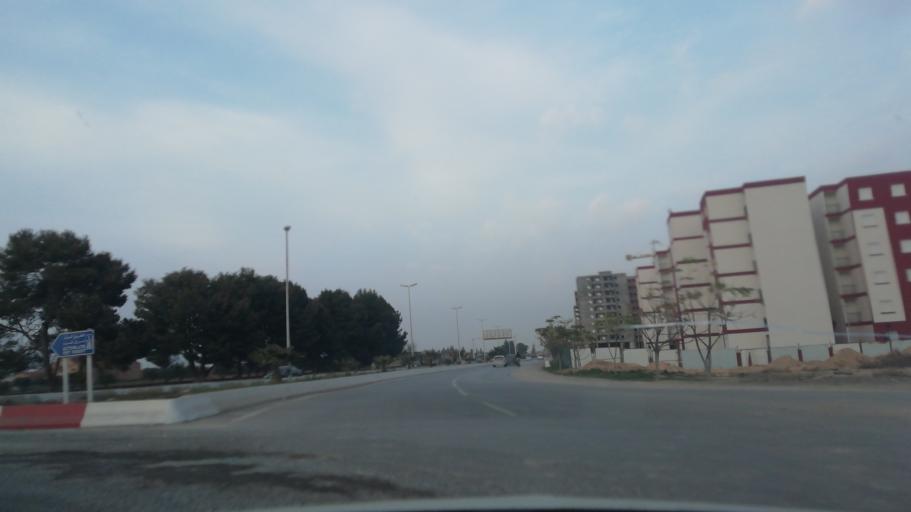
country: DZ
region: Sidi Bel Abbes
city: Sidi Bel Abbes
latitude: 35.2110
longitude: -0.6560
